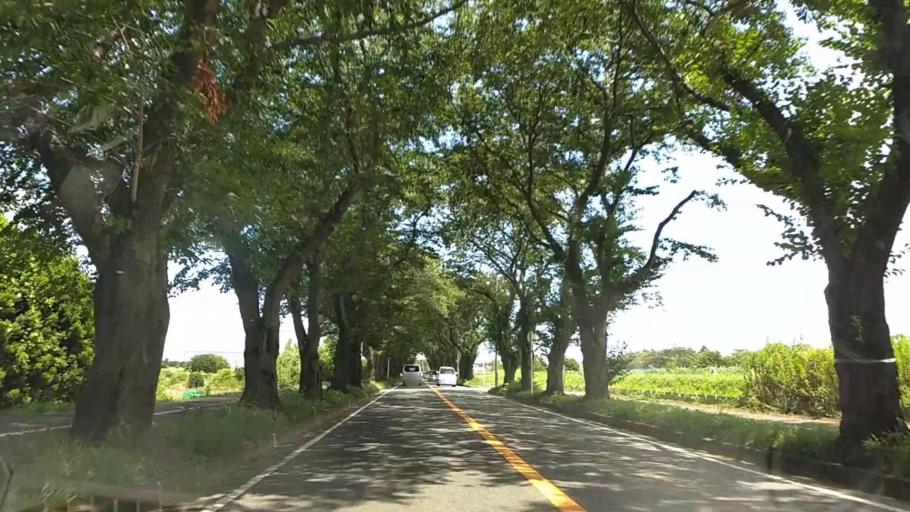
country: JP
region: Kanagawa
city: Minami-rinkan
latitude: 35.4920
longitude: 139.4801
